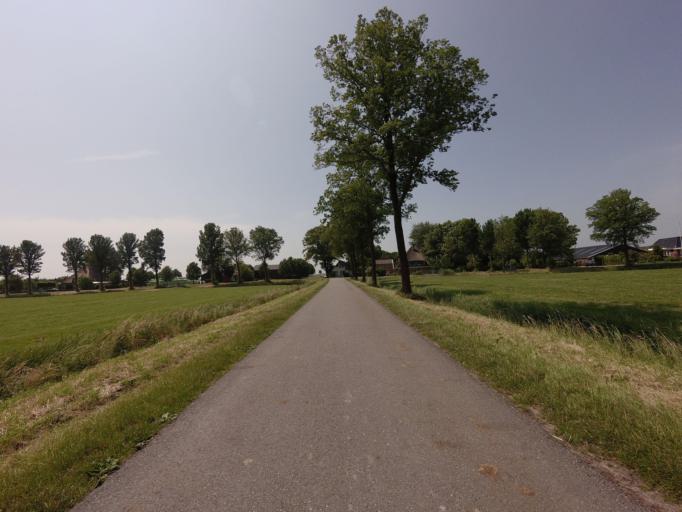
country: NL
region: North Holland
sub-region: Gemeente Opmeer
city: Opmeer
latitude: 52.6849
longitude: 4.9701
